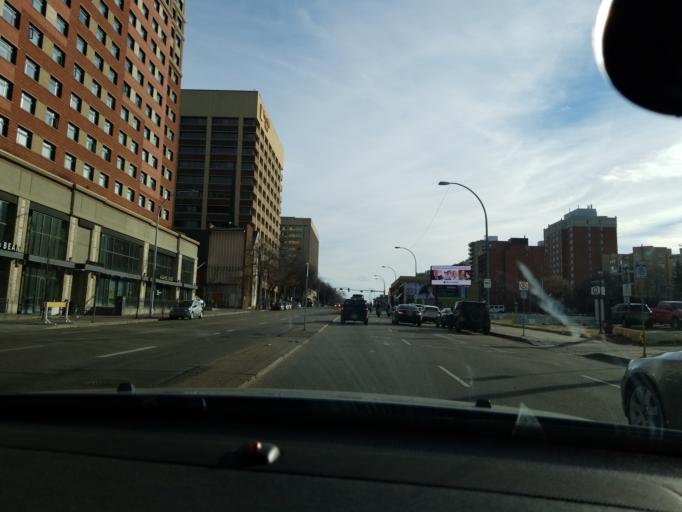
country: CA
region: Alberta
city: Edmonton
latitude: 53.5405
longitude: -113.5085
